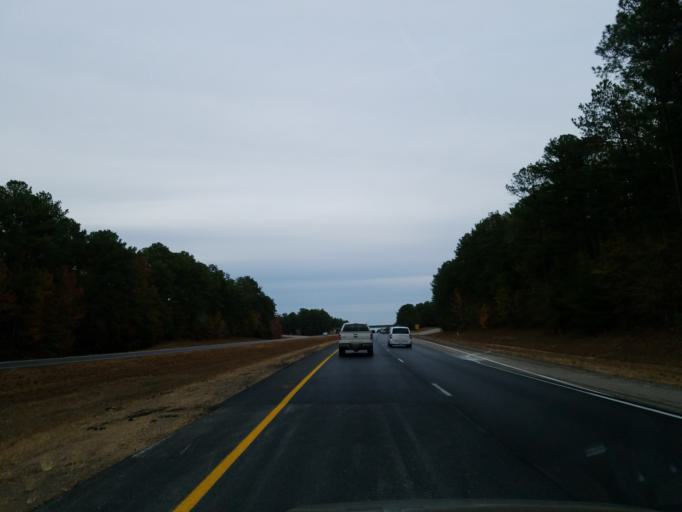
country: US
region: Mississippi
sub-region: Clarke County
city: Stonewall
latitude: 32.2633
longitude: -88.8170
